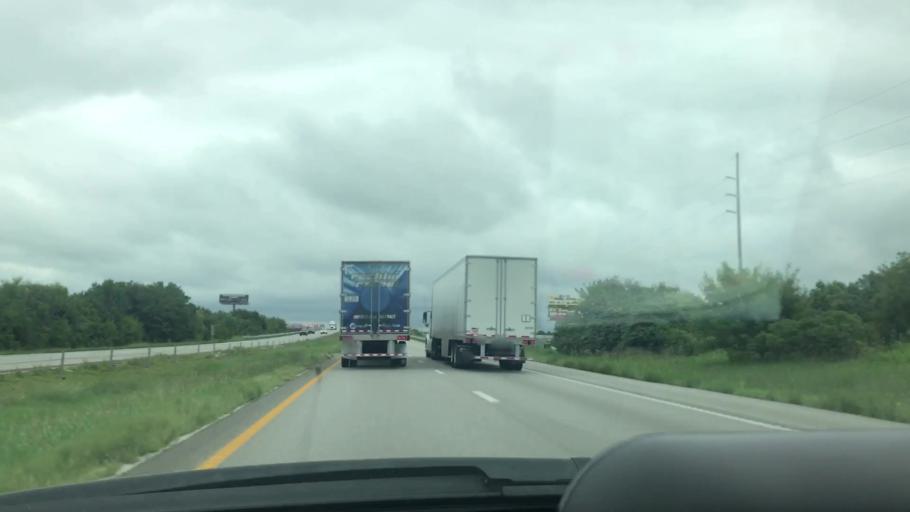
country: US
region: Missouri
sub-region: Greene County
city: Springfield
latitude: 37.2171
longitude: -93.3801
